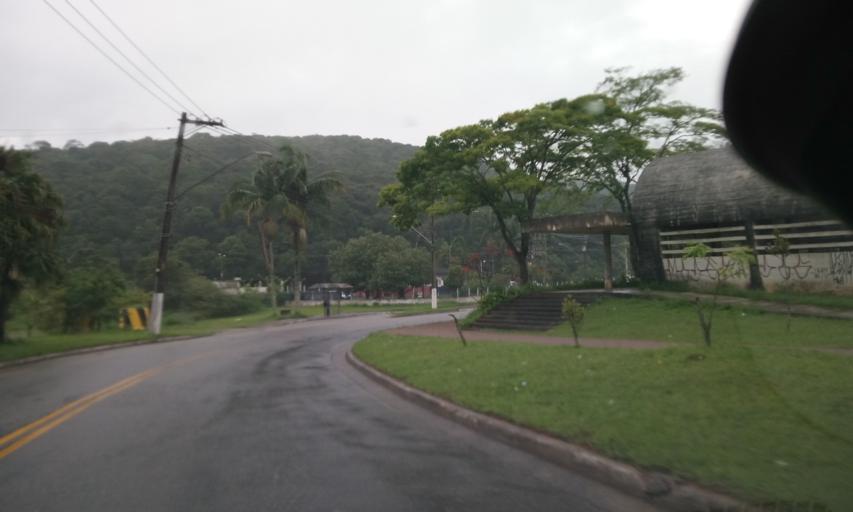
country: BR
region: Sao Paulo
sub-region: Maua
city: Maua
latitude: -23.7295
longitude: -46.4956
